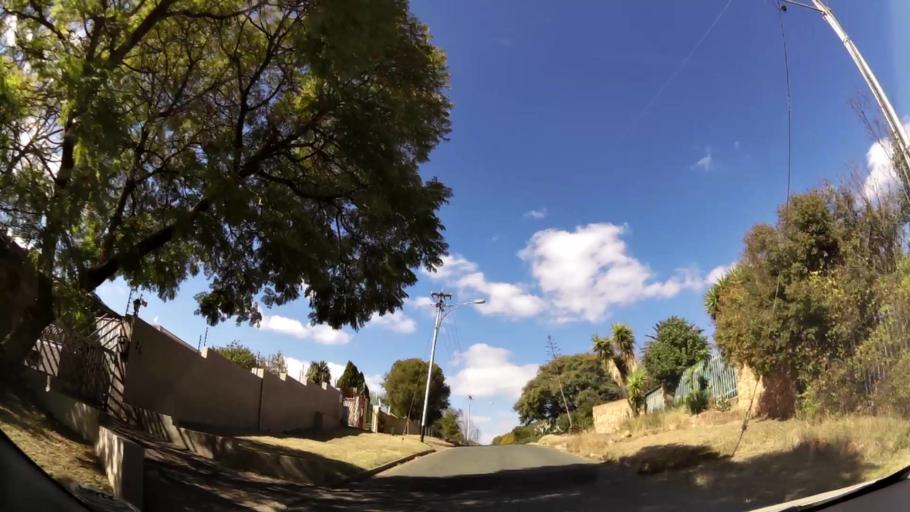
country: ZA
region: Gauteng
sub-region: West Rand District Municipality
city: Krugersdorp
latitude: -26.0947
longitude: 27.7838
